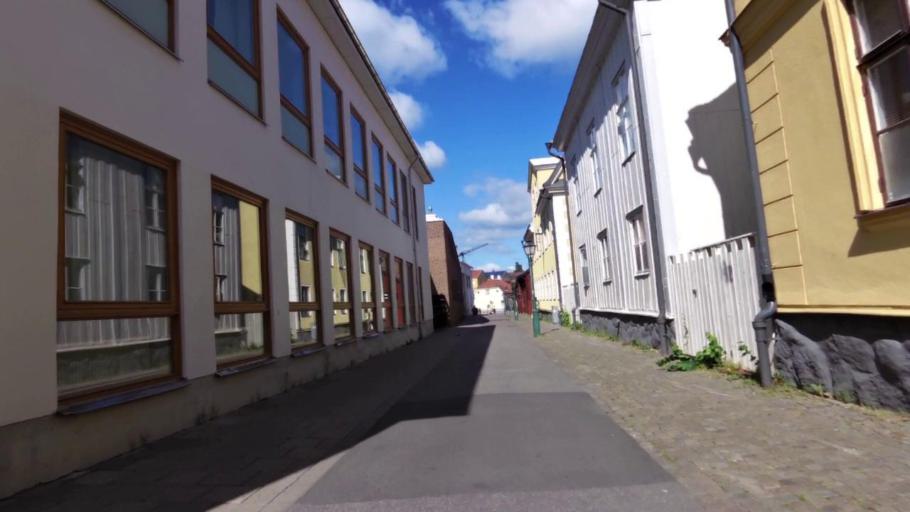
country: SE
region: OEstergoetland
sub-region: Linkopings Kommun
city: Linkoping
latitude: 58.4119
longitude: 15.6146
